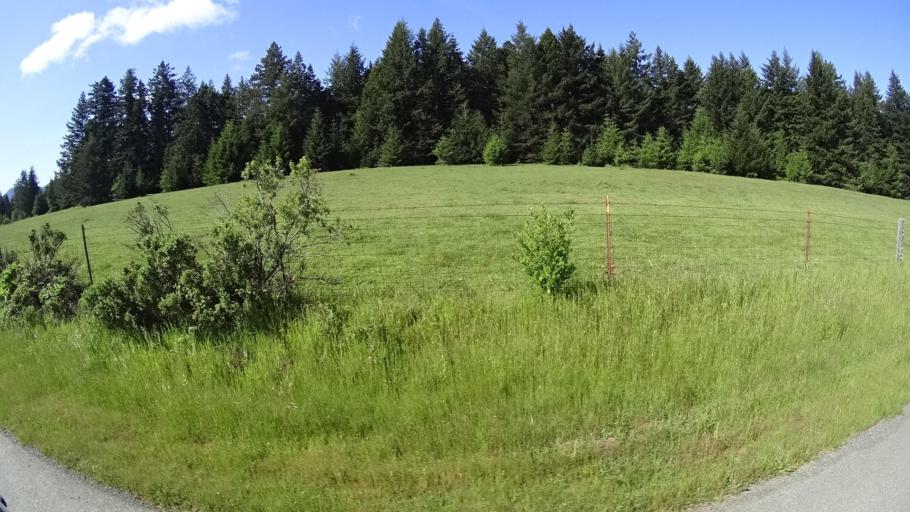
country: US
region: California
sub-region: Humboldt County
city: Ferndale
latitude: 40.3434
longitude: -124.3228
